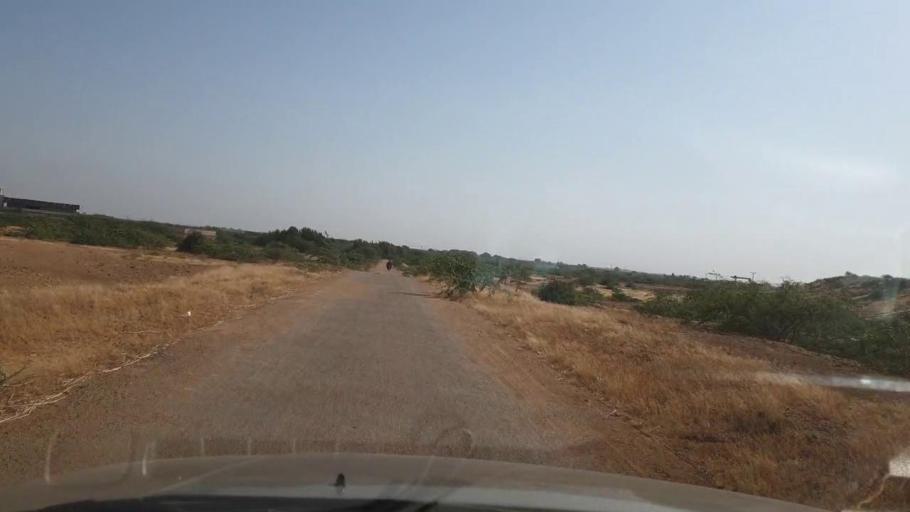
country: PK
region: Sindh
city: Daro Mehar
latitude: 24.9956
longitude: 68.1510
